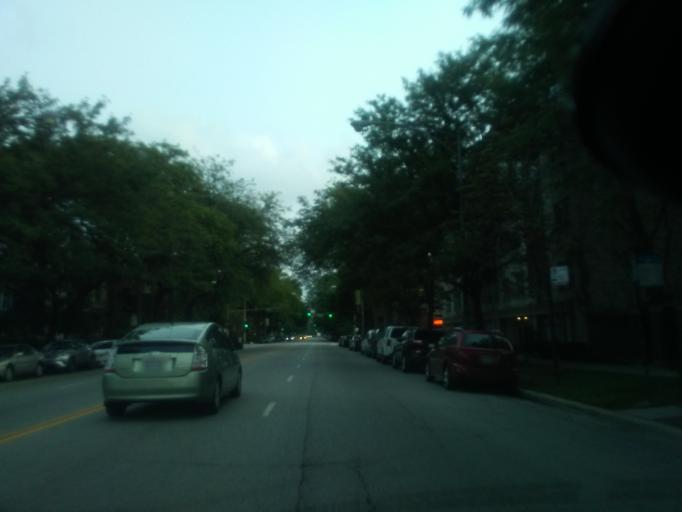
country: US
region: Illinois
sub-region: Cook County
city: Evanston
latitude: 42.0070
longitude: -87.6613
